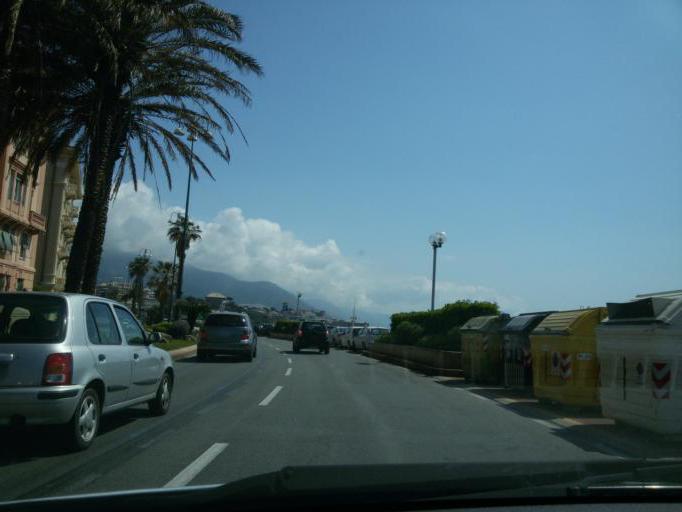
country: IT
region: Liguria
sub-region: Provincia di Genova
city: San Teodoro
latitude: 44.3916
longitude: 8.9558
